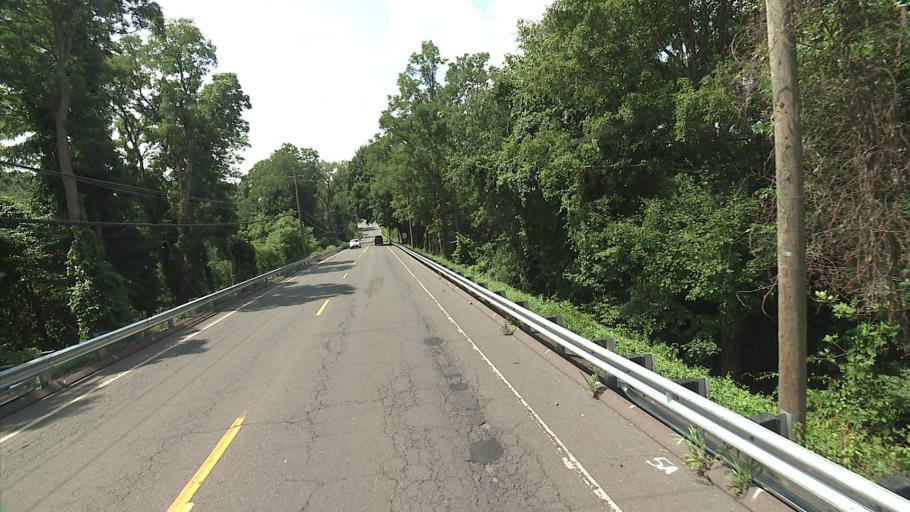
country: US
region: Connecticut
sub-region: Middlesex County
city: Cromwell
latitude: 41.6106
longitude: -72.6010
